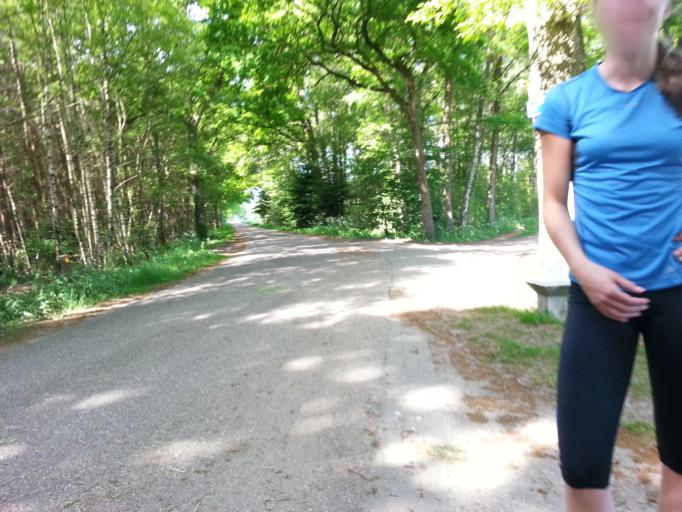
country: NL
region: Gelderland
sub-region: Berkelland
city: Eibergen
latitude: 52.1189
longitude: 6.6910
